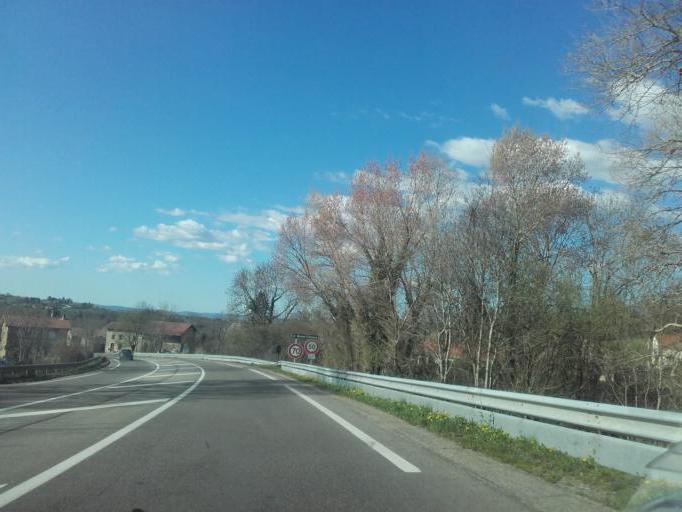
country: FR
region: Rhone-Alpes
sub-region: Departement de l'Isere
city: Nivolas-Vermelle
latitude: 45.5170
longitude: 5.3058
